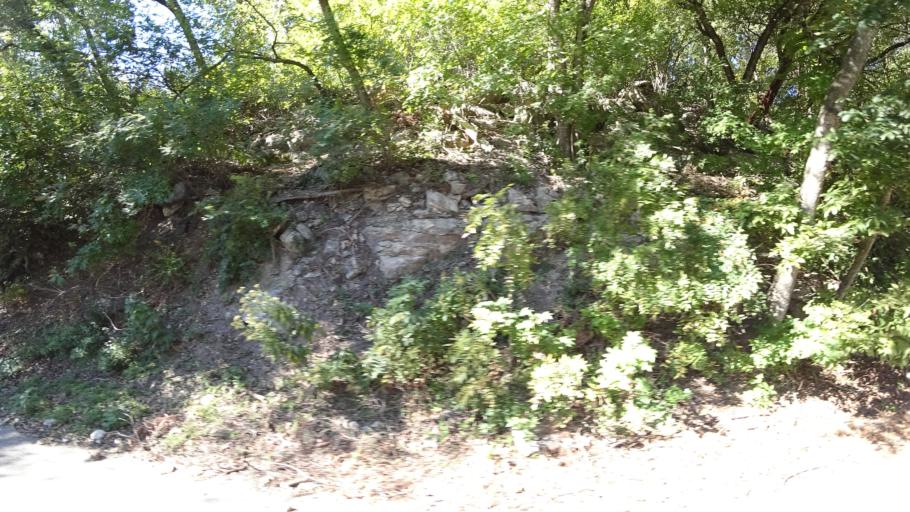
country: US
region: Texas
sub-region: Travis County
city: West Lake Hills
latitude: 30.3321
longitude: -97.7829
